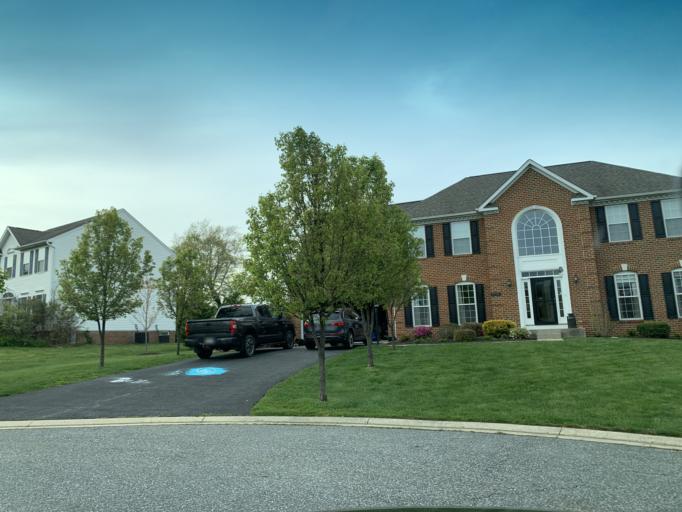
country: US
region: Maryland
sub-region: Harford County
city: Pleasant Hills
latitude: 39.4879
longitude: -76.3696
